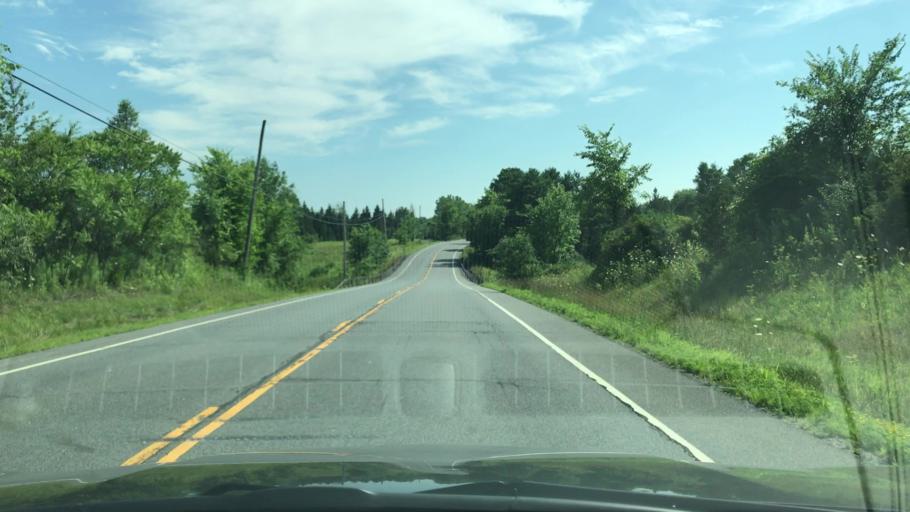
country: US
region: New York
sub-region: Washington County
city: Whitehall
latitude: 43.5123
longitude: -73.4168
